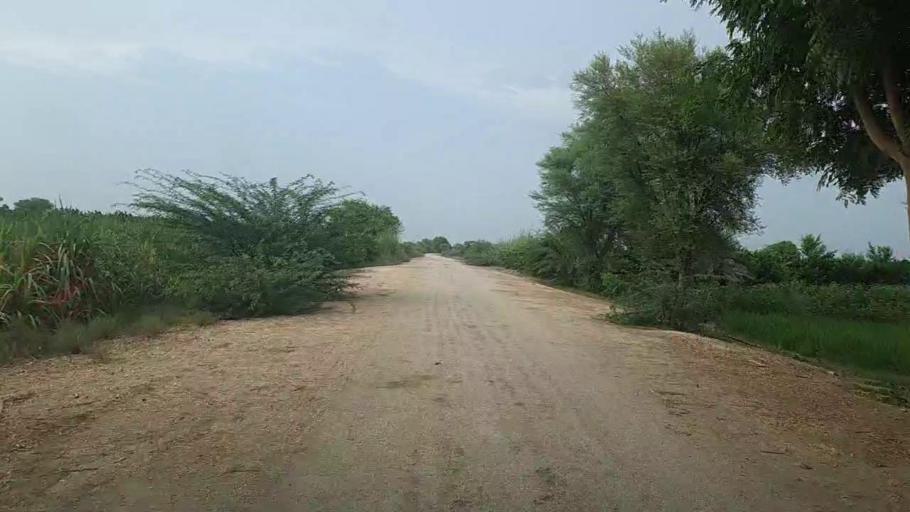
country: PK
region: Sindh
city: Karaundi
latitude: 26.9792
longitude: 68.4339
